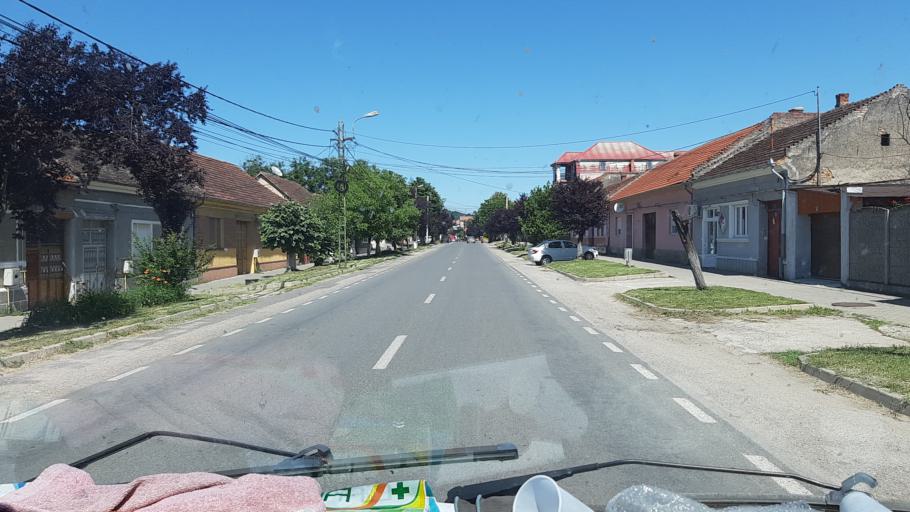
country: RO
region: Caras-Severin
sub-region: Oras Bocsa
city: Bocsa
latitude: 45.3761
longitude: 21.7167
